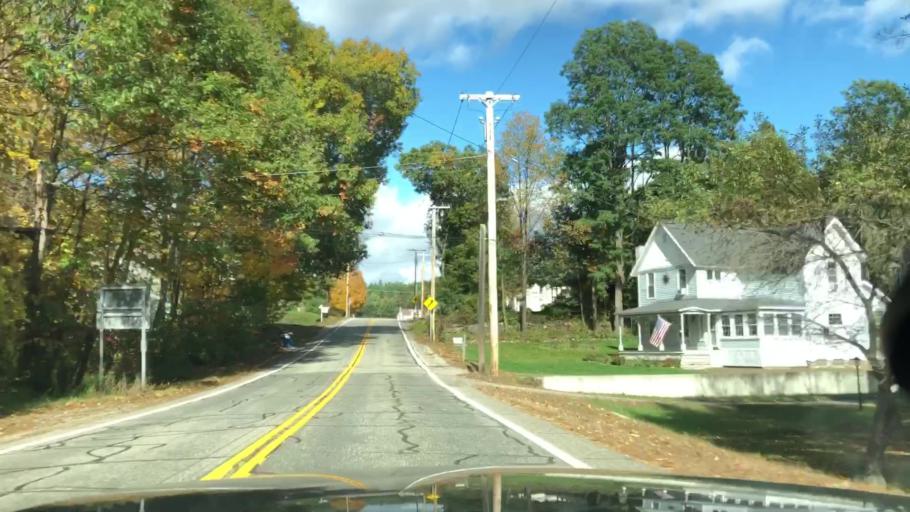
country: US
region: New York
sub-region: Warren County
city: Warrensburg
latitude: 43.7011
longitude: -73.9827
